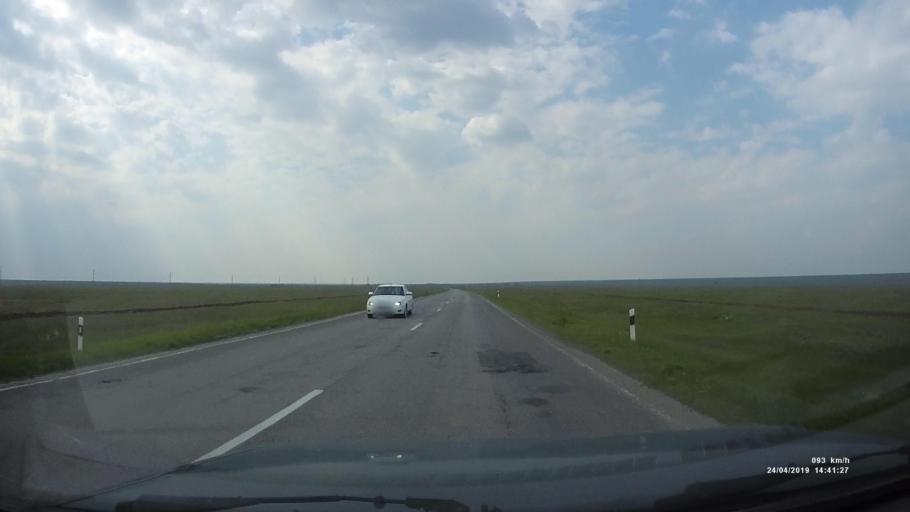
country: RU
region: Rostov
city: Remontnoye
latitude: 46.4450
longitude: 43.8798
